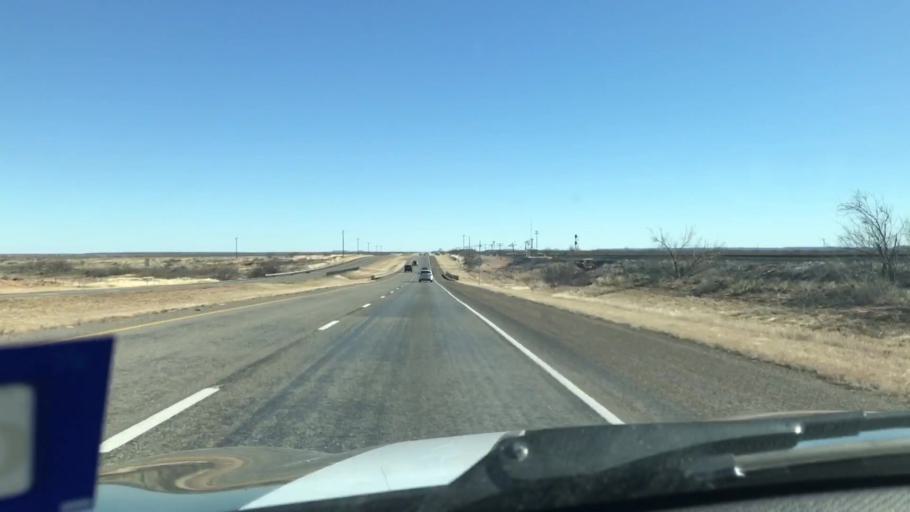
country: US
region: Texas
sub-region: Garza County
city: Post
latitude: 33.1368
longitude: -101.3110
